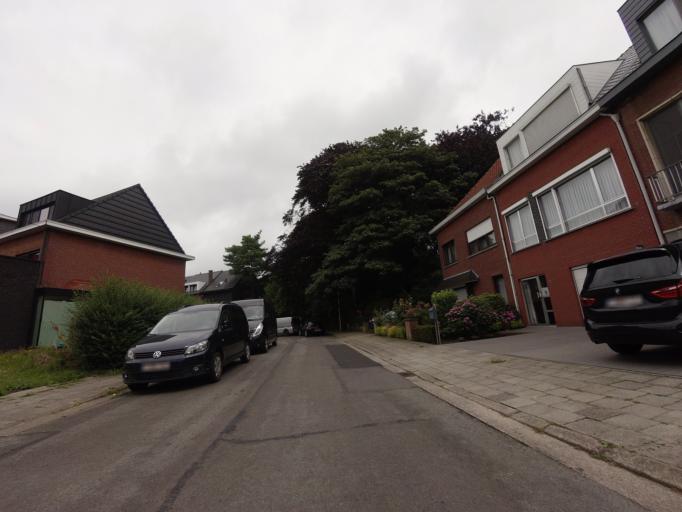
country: BE
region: Flanders
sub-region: Provincie Antwerpen
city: Edegem
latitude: 51.1551
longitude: 4.4396
